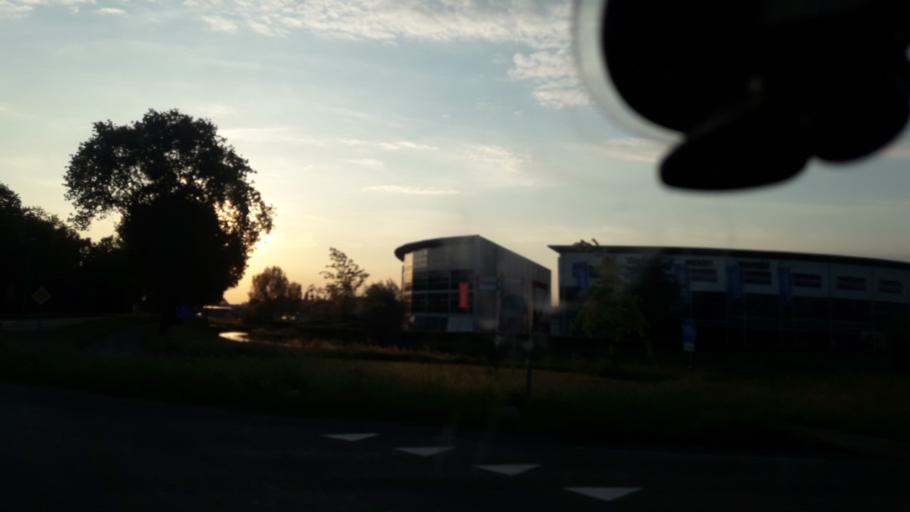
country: NL
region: Gelderland
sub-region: Gemeente Elburg
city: Elburg
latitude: 52.4403
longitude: 5.8658
